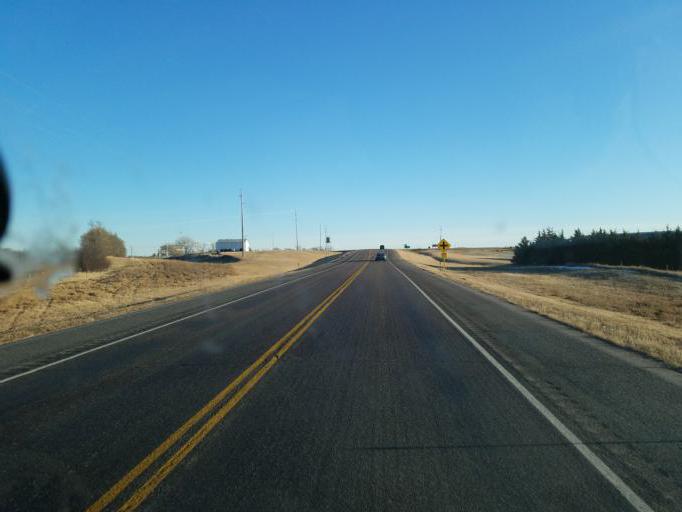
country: US
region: South Dakota
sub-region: Hutchinson County
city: Parkston
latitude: 43.2282
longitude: -97.9791
